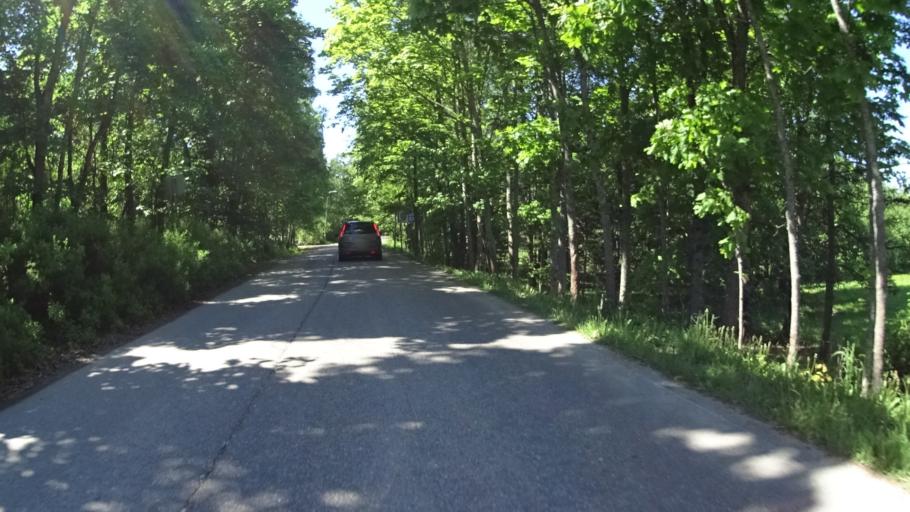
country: FI
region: Uusimaa
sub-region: Helsinki
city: Kilo
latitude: 60.2623
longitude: 24.7699
